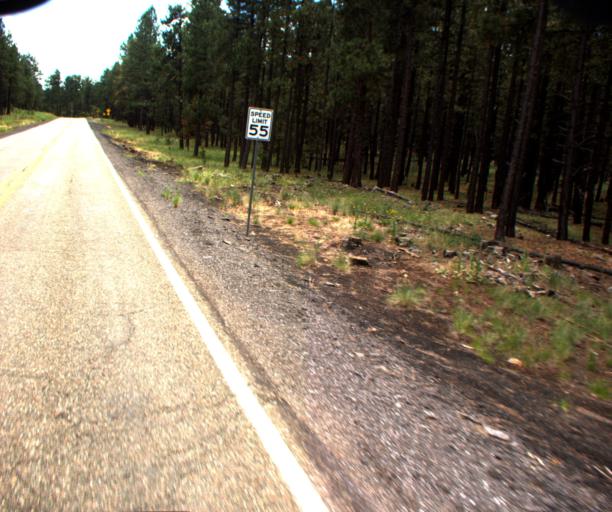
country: US
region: Arizona
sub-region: Coconino County
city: Flagstaff
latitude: 35.3123
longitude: -111.7750
